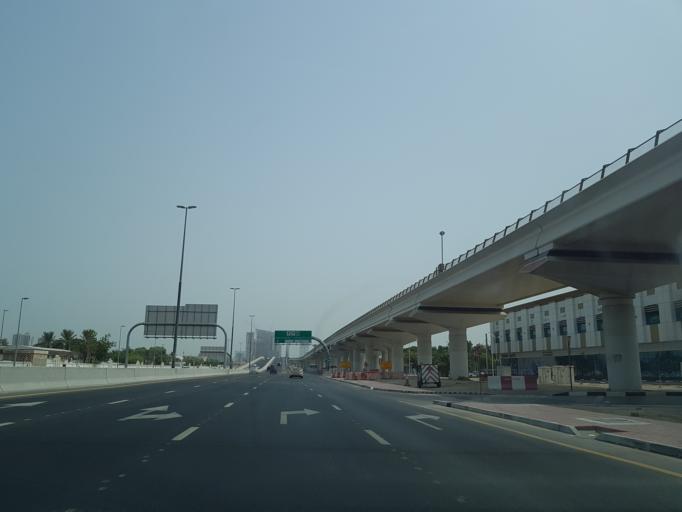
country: AE
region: Ash Shariqah
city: Sharjah
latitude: 25.2348
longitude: 55.2927
